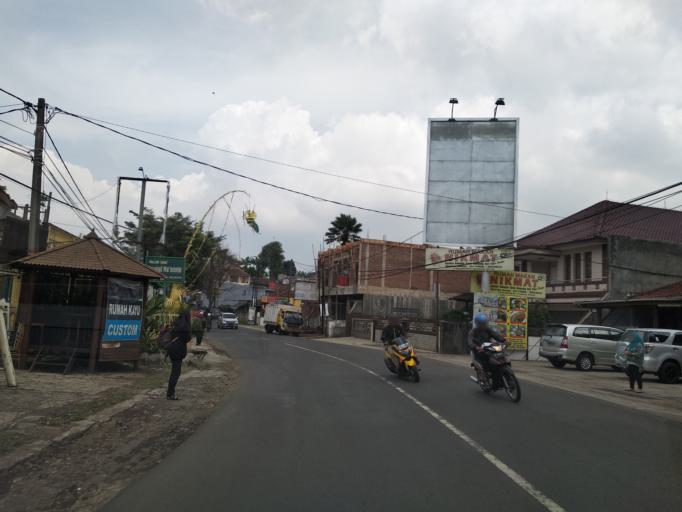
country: ID
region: West Java
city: Lembang
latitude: -6.8216
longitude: 107.6097
